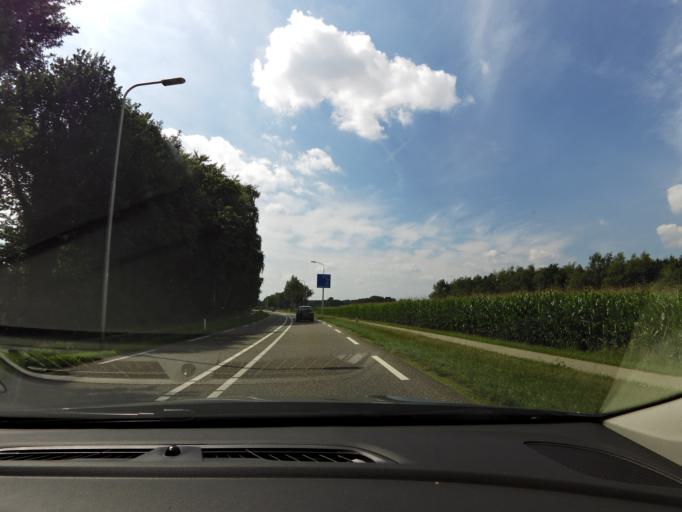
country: NL
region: Limburg
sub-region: Gemeente Roerdalen
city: Herkenbosch
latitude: 51.1600
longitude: 6.0710
